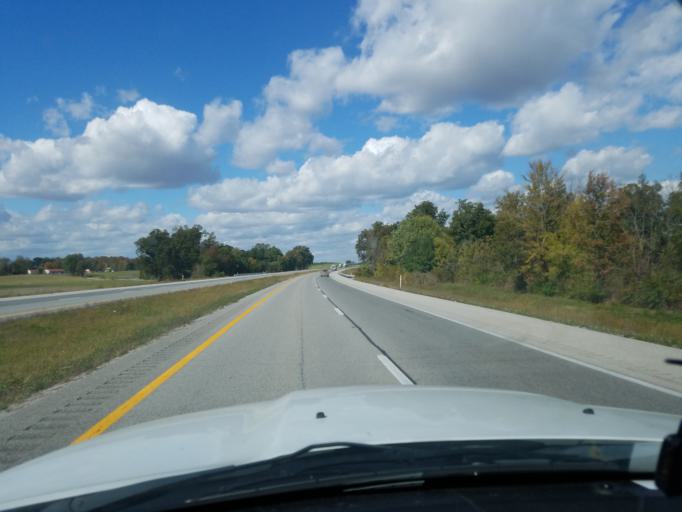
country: US
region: Kentucky
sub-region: Daviess County
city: Masonville
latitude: 37.6666
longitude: -87.0208
